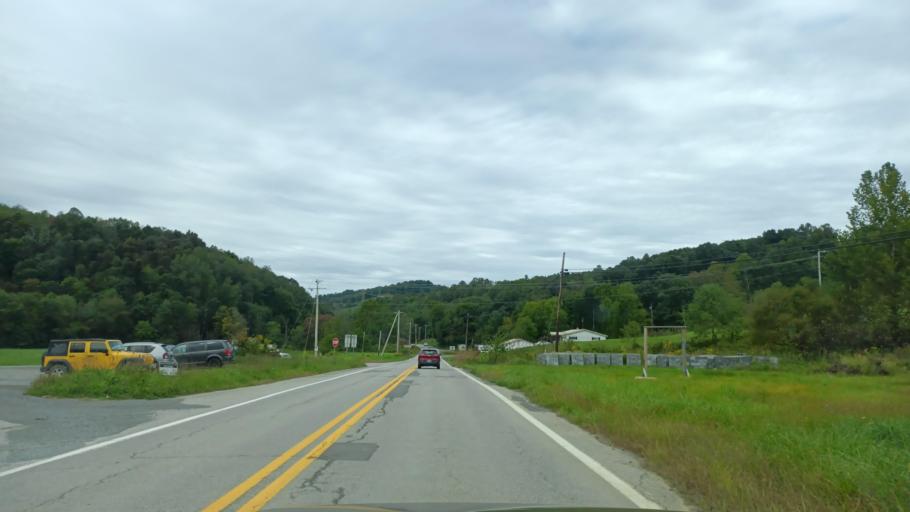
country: US
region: West Virginia
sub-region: Taylor County
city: Grafton
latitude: 39.3316
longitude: -79.8478
